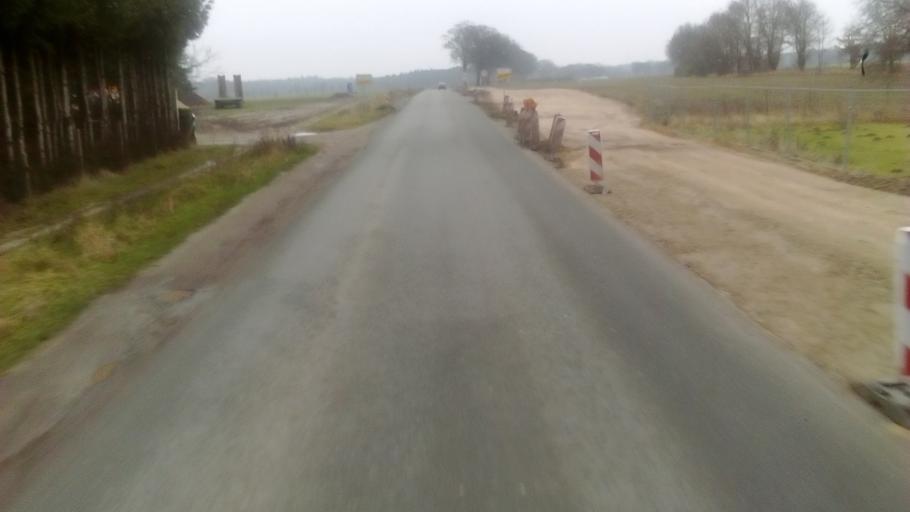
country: DE
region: Brandenburg
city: Gross Pankow
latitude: 53.1236
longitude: 12.0474
